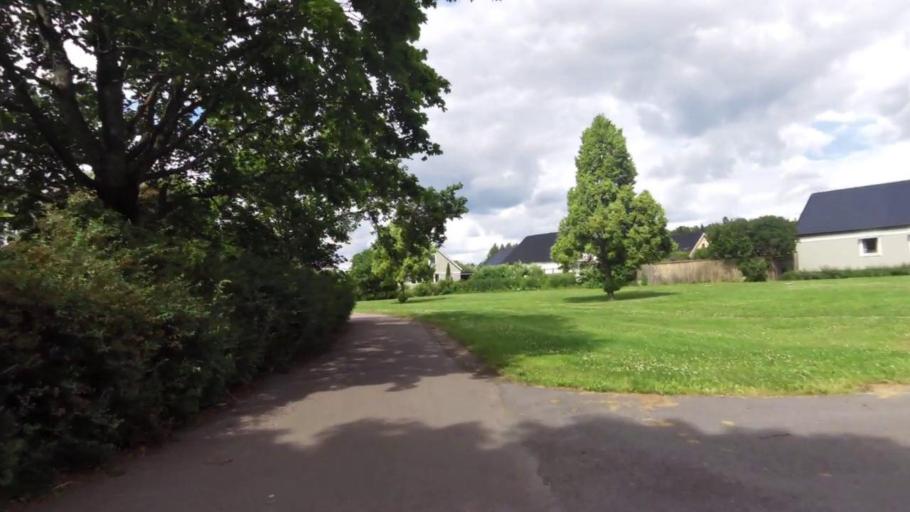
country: SE
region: OEstergoetland
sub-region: Linkopings Kommun
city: Malmslatt
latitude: 58.4148
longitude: 15.5642
